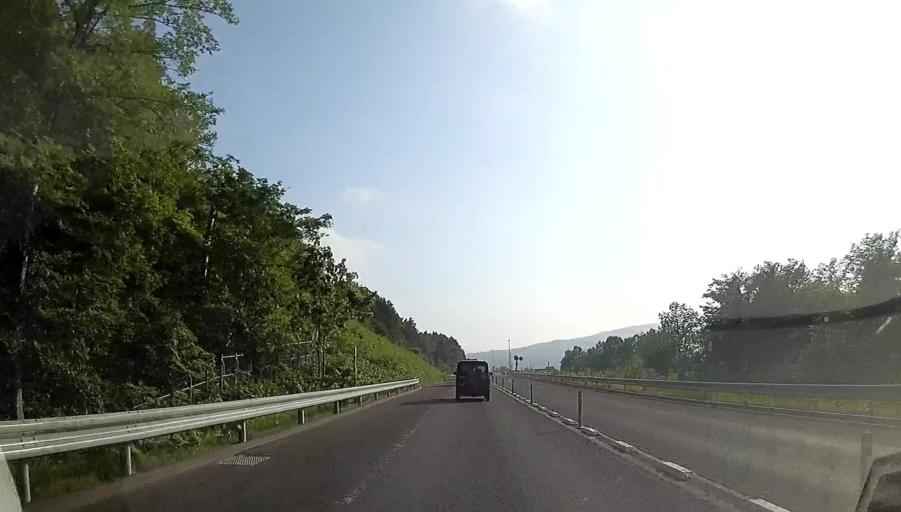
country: JP
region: Hokkaido
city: Shimo-furano
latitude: 43.0114
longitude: 142.4269
